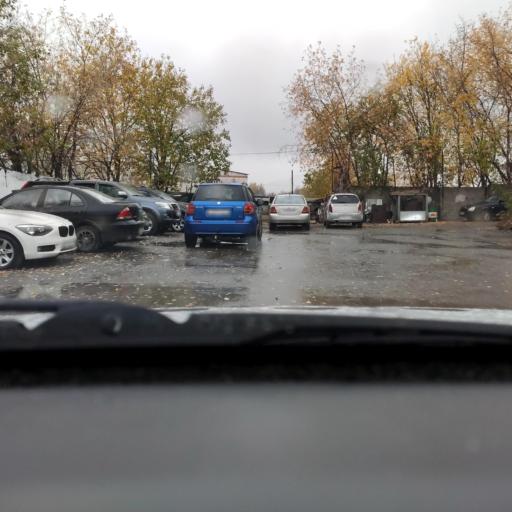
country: RU
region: Perm
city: Perm
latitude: 58.0227
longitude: 56.2822
